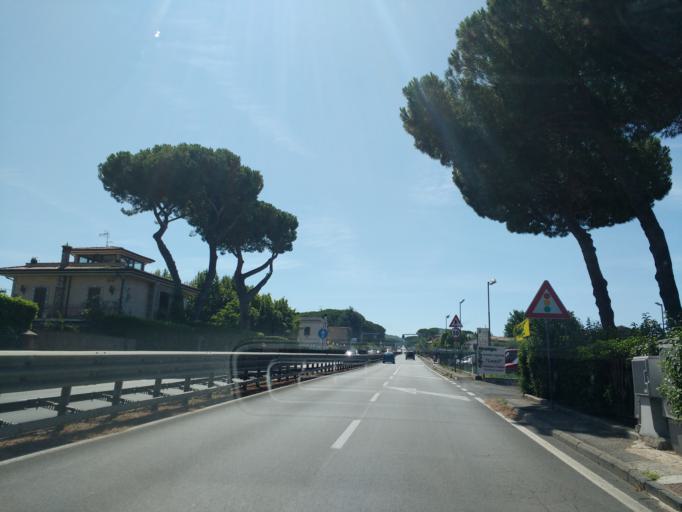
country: IT
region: Latium
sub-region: Citta metropolitana di Roma Capitale
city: Marino
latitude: 41.7626
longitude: 12.6208
